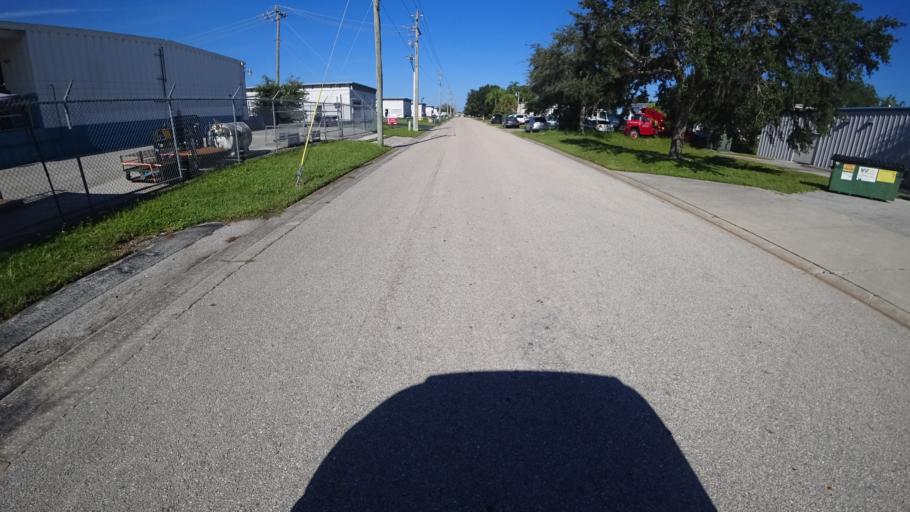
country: US
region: Florida
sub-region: Manatee County
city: Whitfield
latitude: 27.4189
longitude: -82.5345
